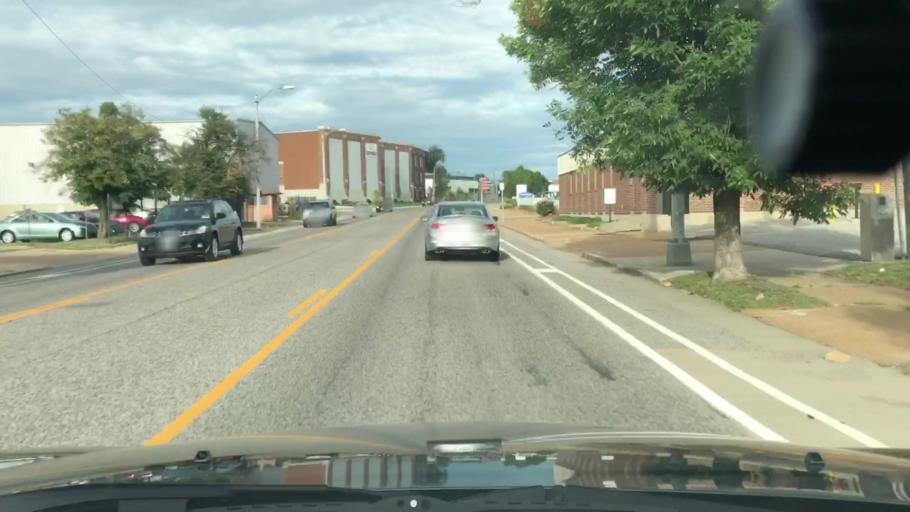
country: US
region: Missouri
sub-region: Saint Louis County
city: Richmond Heights
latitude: 38.6250
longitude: -90.2694
